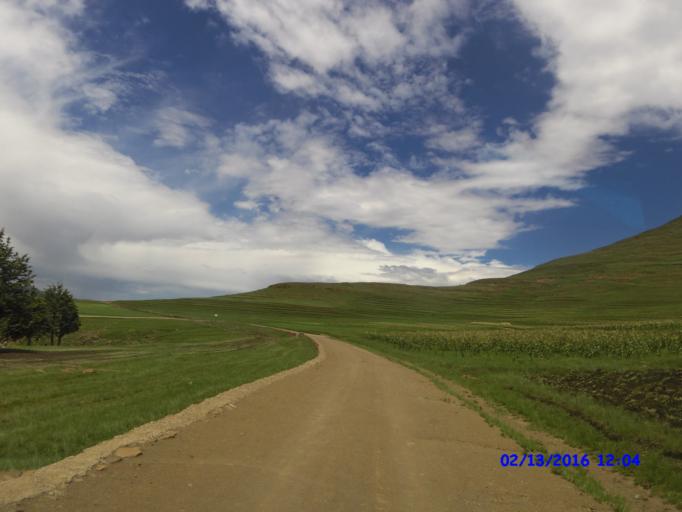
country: LS
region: Maseru
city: Nako
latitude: -29.8758
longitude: 28.0429
